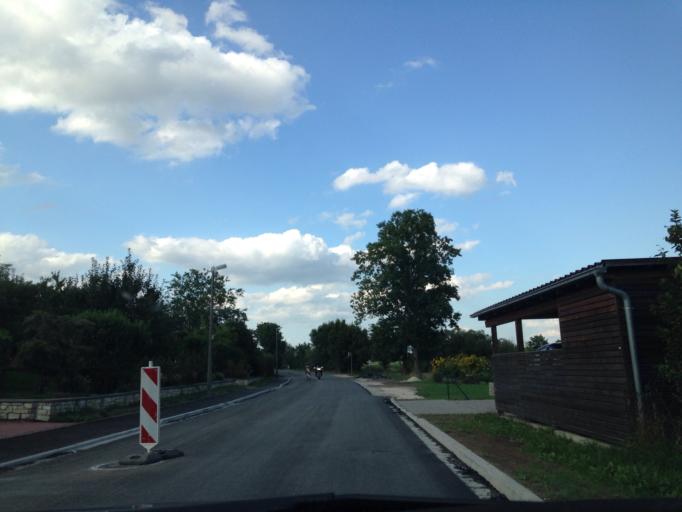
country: DE
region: Bavaria
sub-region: Regierungsbezirk Mittelfranken
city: Greding
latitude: 49.1150
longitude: 11.3104
